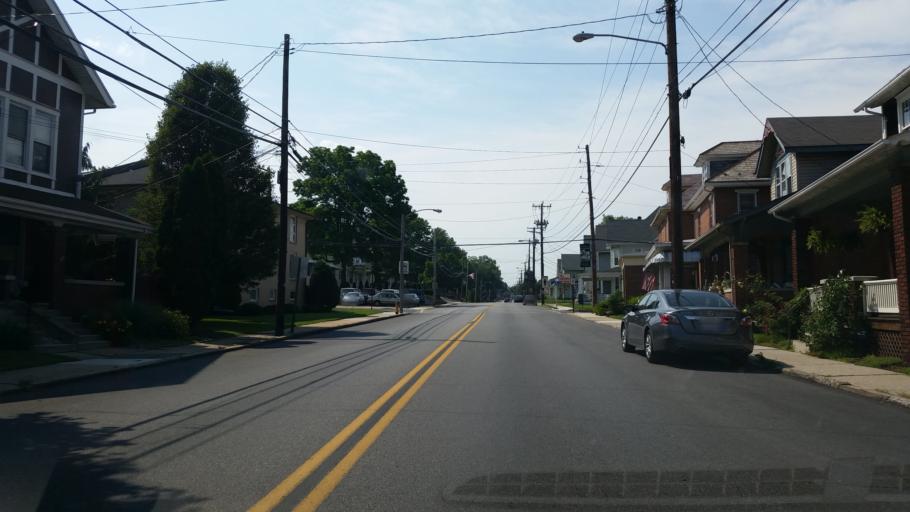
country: US
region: Pennsylvania
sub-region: Cumberland County
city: New Cumberland
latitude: 40.2318
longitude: -76.8724
